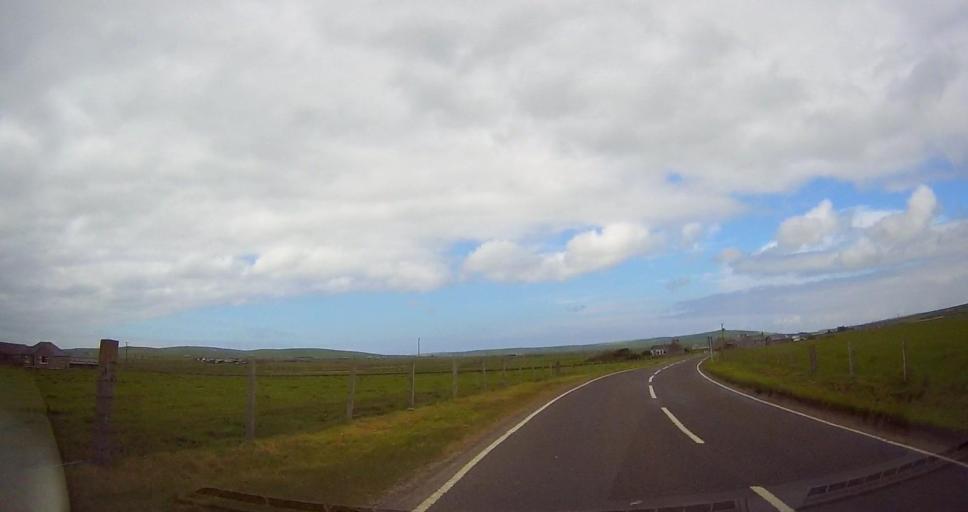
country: GB
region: Scotland
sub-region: Orkney Islands
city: Stromness
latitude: 59.0751
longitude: -3.2472
